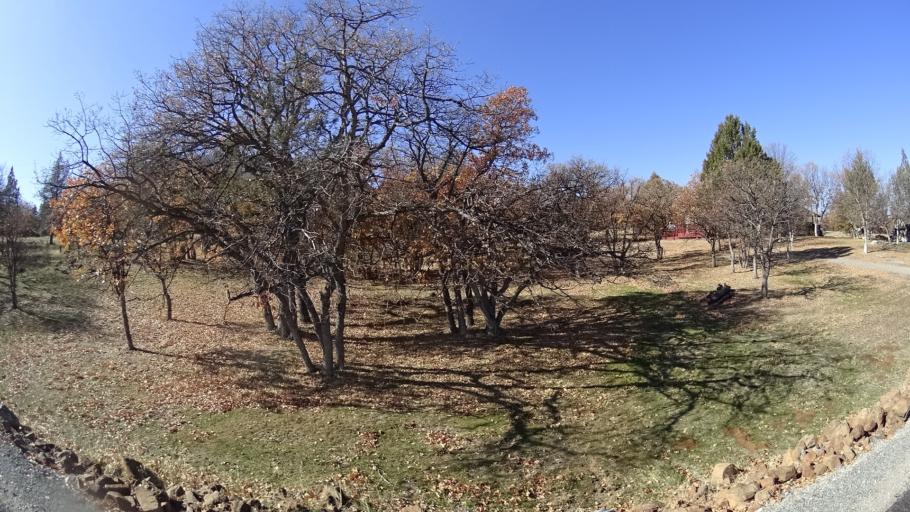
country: US
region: California
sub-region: Siskiyou County
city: Montague
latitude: 41.8787
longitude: -122.4822
